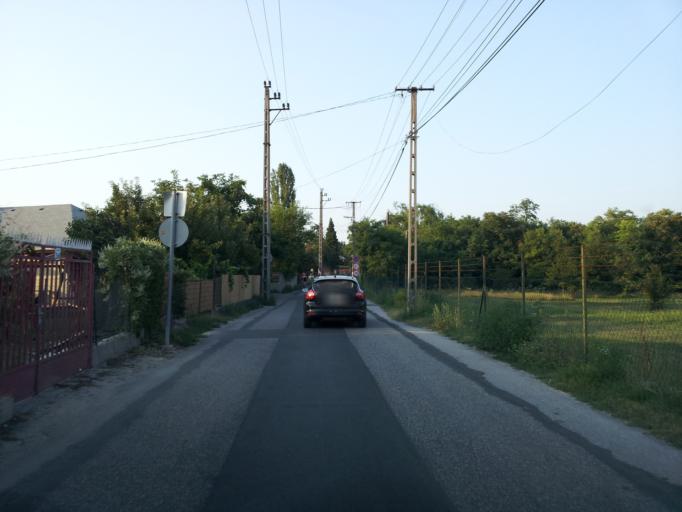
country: HU
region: Pest
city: Szigethalom
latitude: 47.3140
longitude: 19.0313
